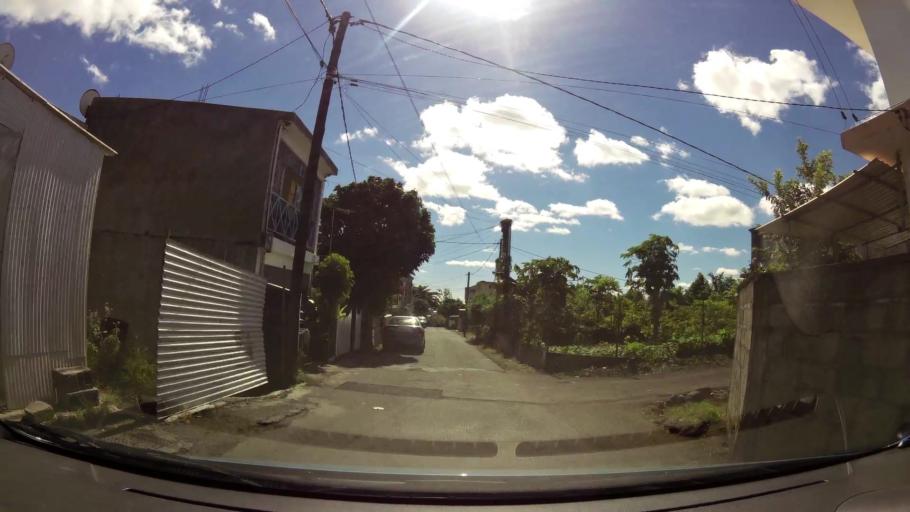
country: MU
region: Plaines Wilhems
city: Vacoas
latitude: -20.3045
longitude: 57.4766
